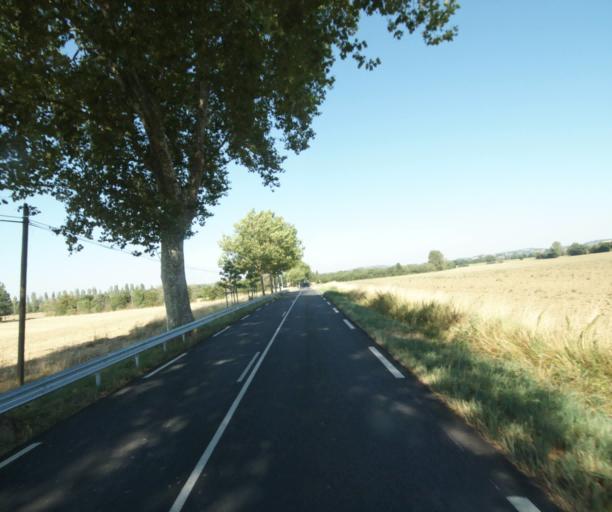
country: FR
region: Midi-Pyrenees
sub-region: Departement de la Haute-Garonne
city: Revel
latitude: 43.4692
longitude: 1.9648
